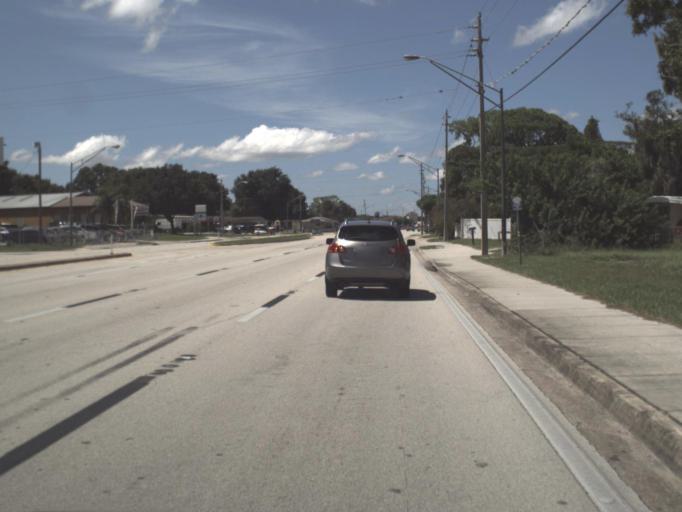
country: US
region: Florida
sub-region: Polk County
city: Auburndale
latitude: 28.0602
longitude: -81.8077
